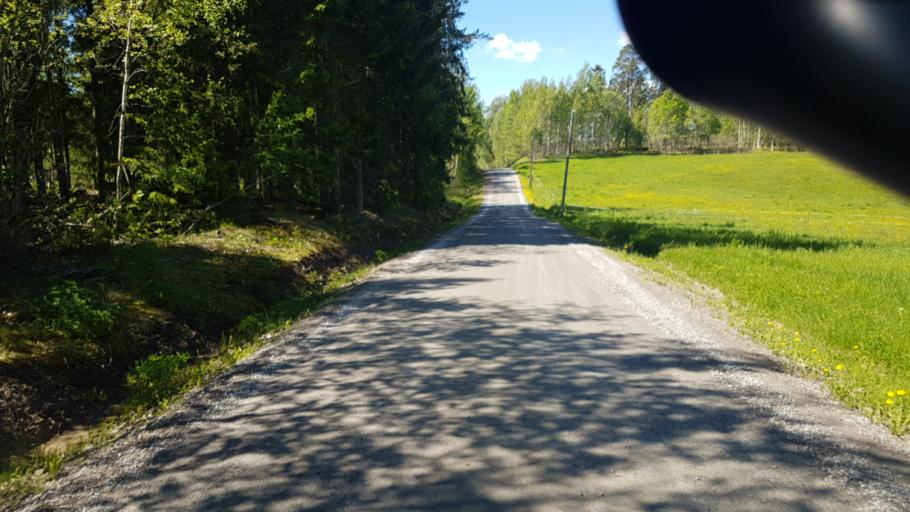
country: SE
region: Vaermland
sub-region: Arvika Kommun
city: Arvika
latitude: 59.6018
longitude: 12.7683
